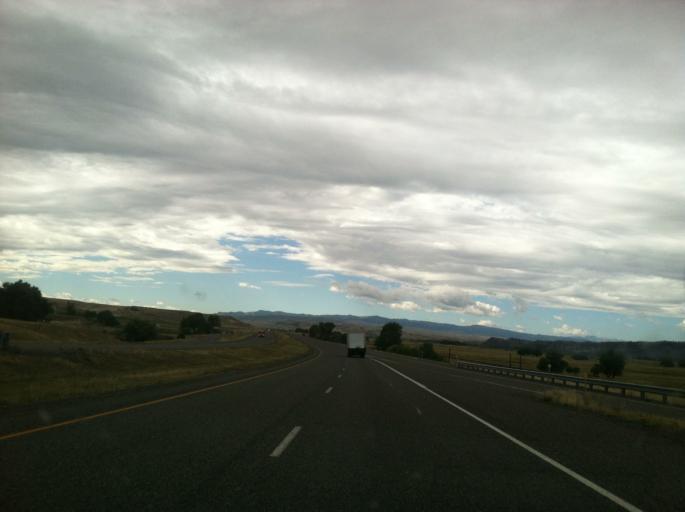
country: US
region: Montana
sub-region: Park County
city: Livingston
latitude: 45.7136
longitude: -110.4023
